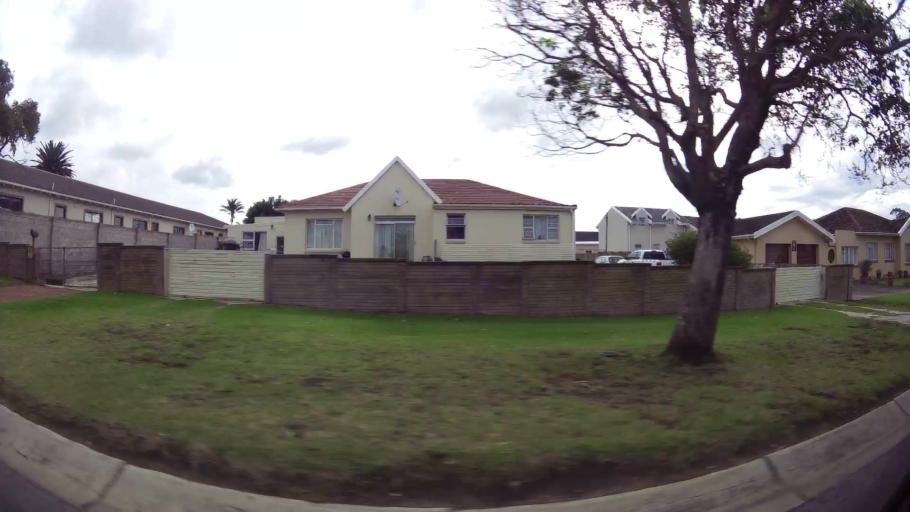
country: ZA
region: Eastern Cape
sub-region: Nelson Mandela Bay Metropolitan Municipality
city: Port Elizabeth
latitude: -33.9416
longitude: 25.5232
